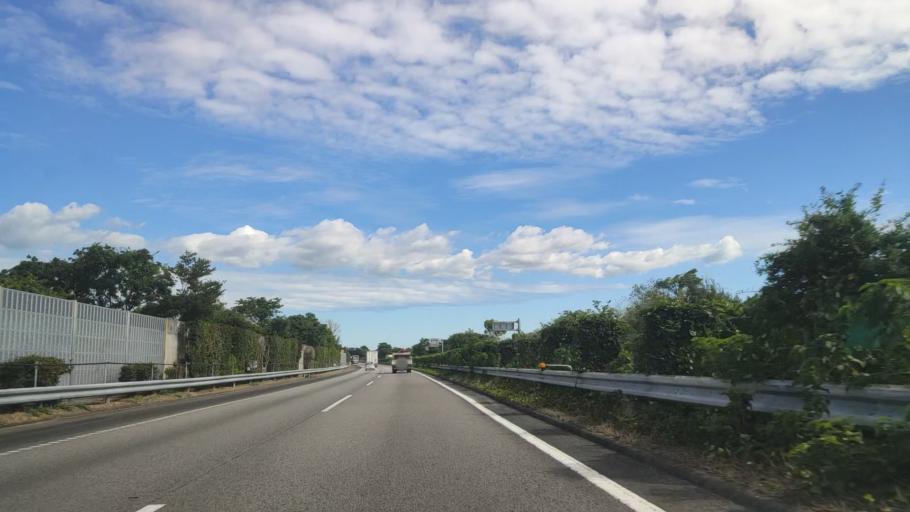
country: JP
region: Shizuoka
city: Hamamatsu
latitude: 34.7527
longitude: 137.7450
